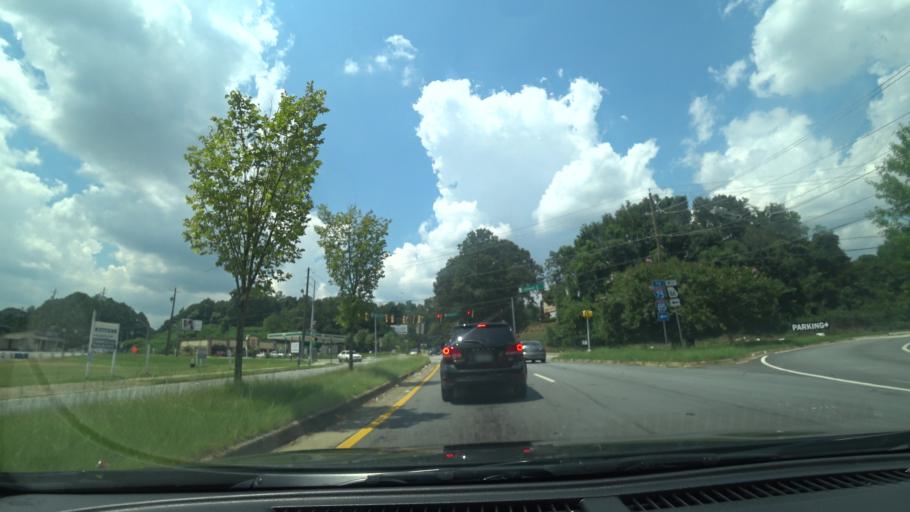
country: US
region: Georgia
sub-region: Fulton County
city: Hapeville
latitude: 33.6981
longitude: -84.3925
